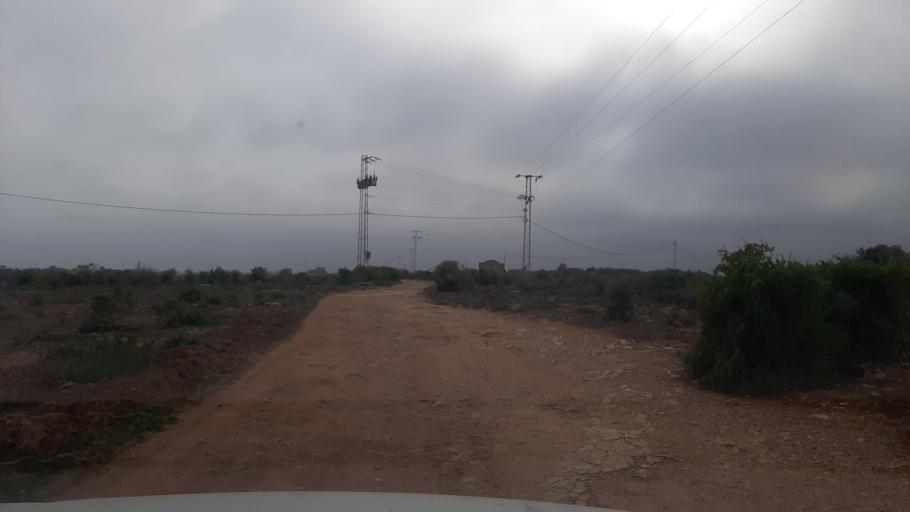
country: TN
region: Nabul
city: Menzel Heurr
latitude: 36.6902
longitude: 10.9333
